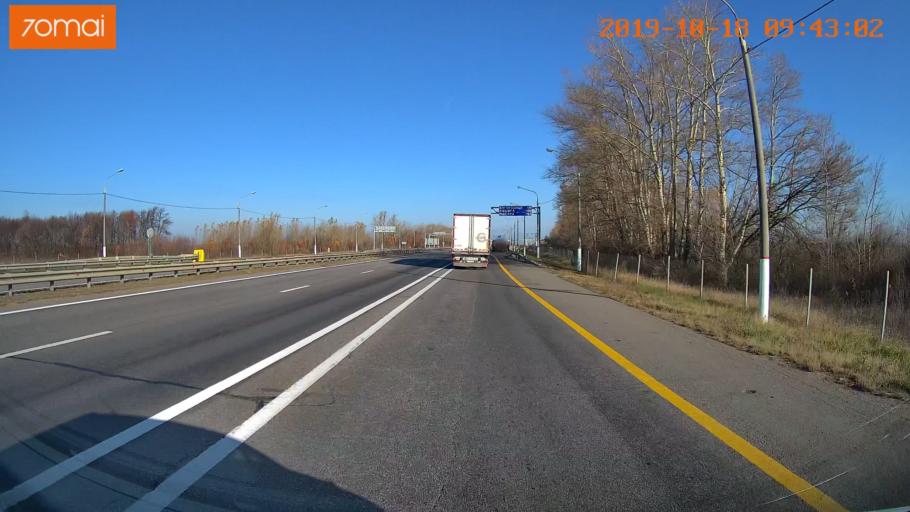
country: RU
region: Tula
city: Kazachka
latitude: 53.2926
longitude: 38.1785
